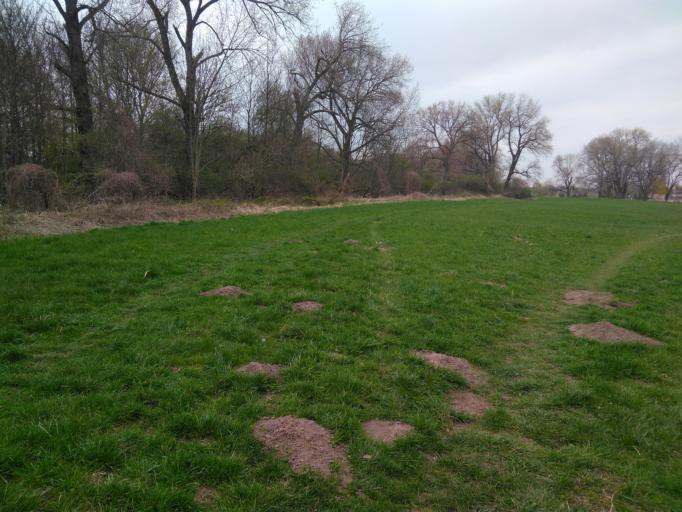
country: DE
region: North Rhine-Westphalia
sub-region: Regierungsbezirk Koln
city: Leverkusen
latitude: 51.0206
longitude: 6.9709
